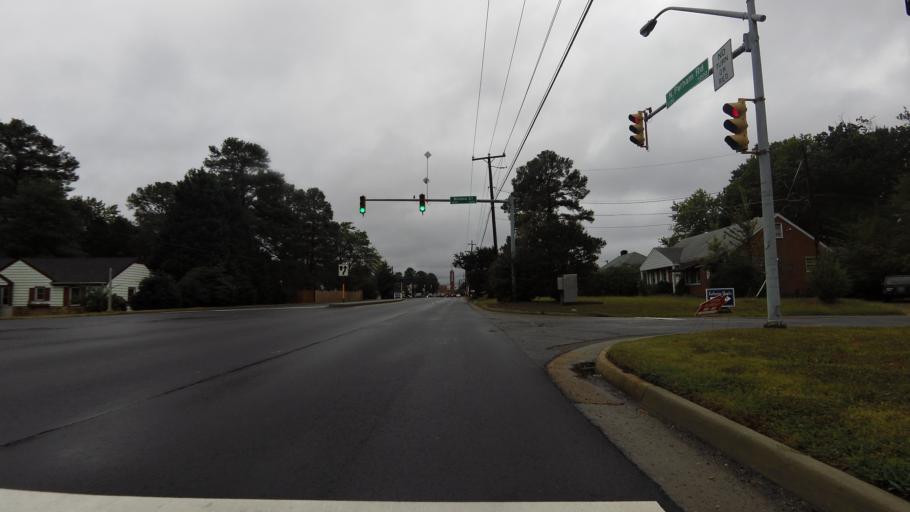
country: US
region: Virginia
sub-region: Henrico County
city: Tuckahoe
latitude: 37.5968
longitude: -77.5654
